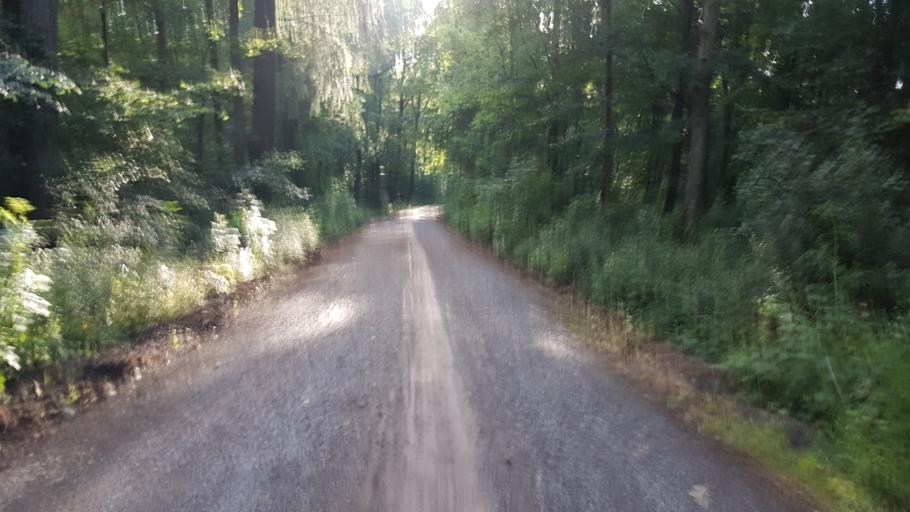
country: DE
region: Baden-Wuerttemberg
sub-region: Karlsruhe Region
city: Sternenfels
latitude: 49.0441
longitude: 8.8893
